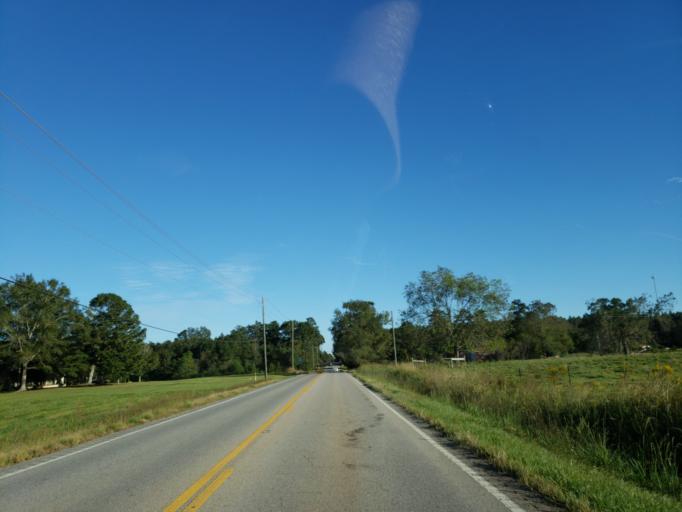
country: US
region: Mississippi
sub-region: Perry County
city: Richton
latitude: 31.3570
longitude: -88.9590
